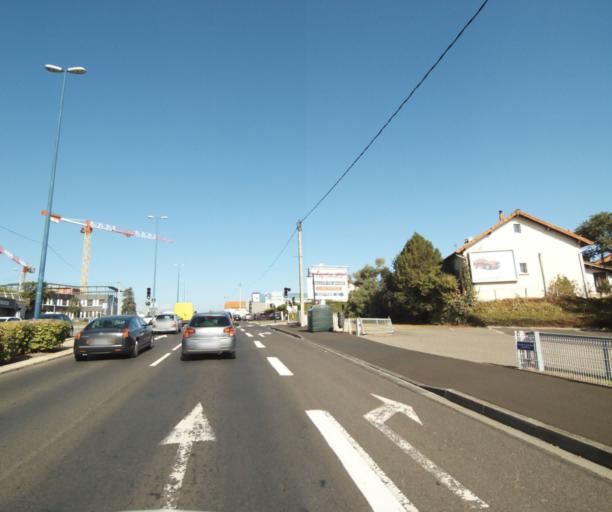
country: FR
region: Auvergne
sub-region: Departement du Puy-de-Dome
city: Aubiere
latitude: 45.7683
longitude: 3.1246
